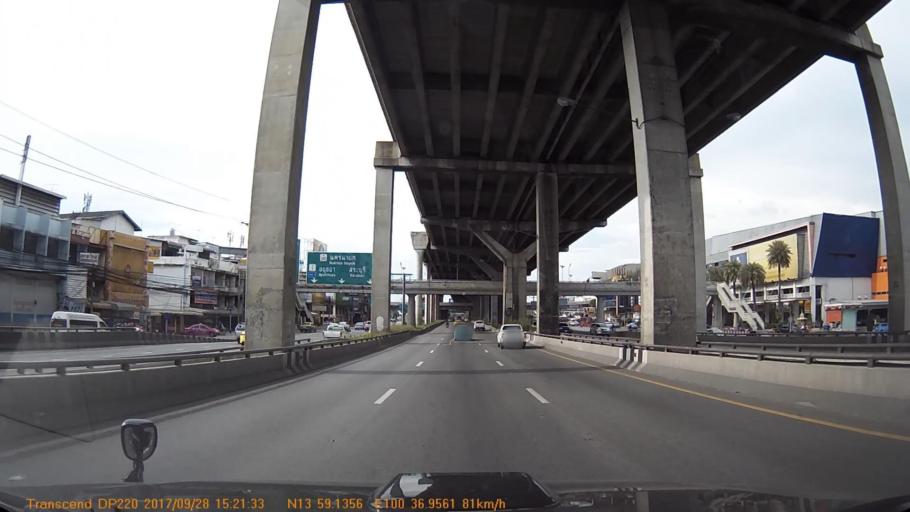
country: TH
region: Phra Nakhon Si Ayutthaya
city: Ban Bang Kadi Pathum Thani
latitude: 13.9858
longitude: 100.6160
